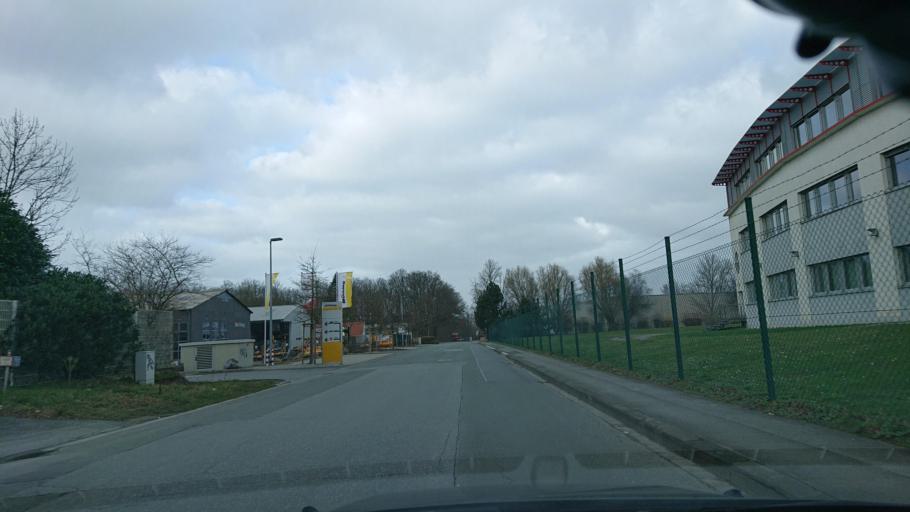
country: DE
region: North Rhine-Westphalia
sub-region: Regierungsbezirk Arnsberg
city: Bad Sassendorf
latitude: 51.5592
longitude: 8.1394
